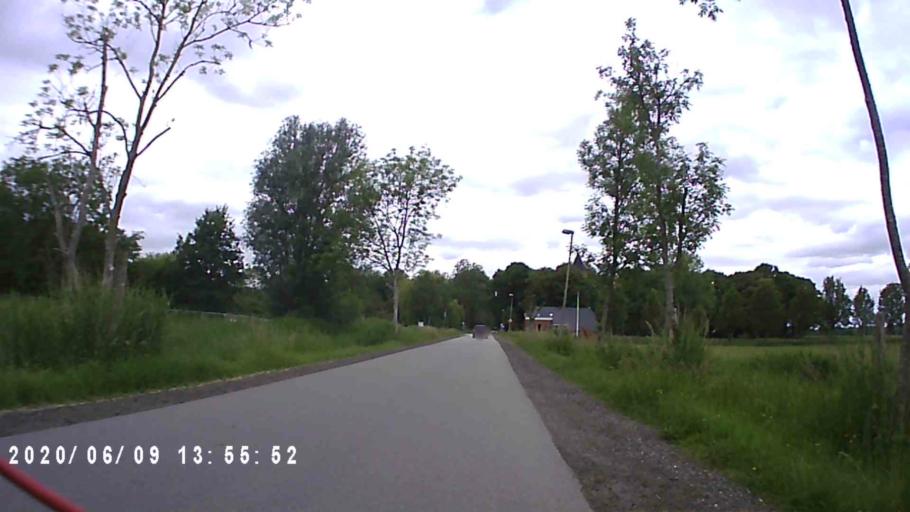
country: NL
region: Groningen
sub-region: Gemeente Groningen
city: Oosterpark
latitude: 53.2428
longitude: 6.6285
